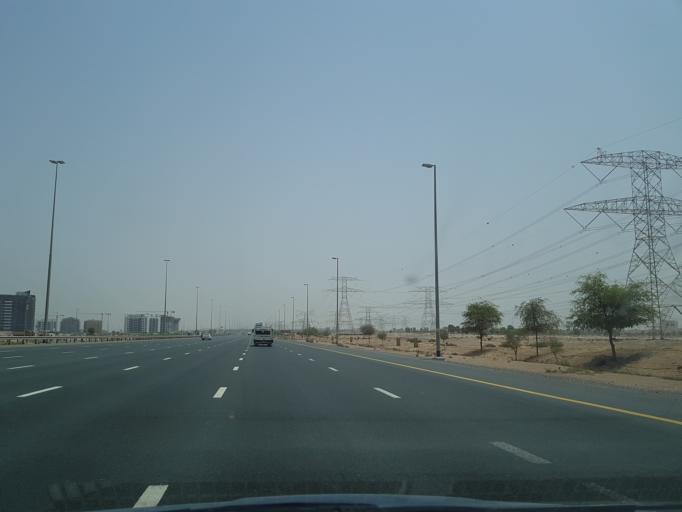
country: AE
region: Dubai
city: Dubai
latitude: 25.0796
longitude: 55.3813
